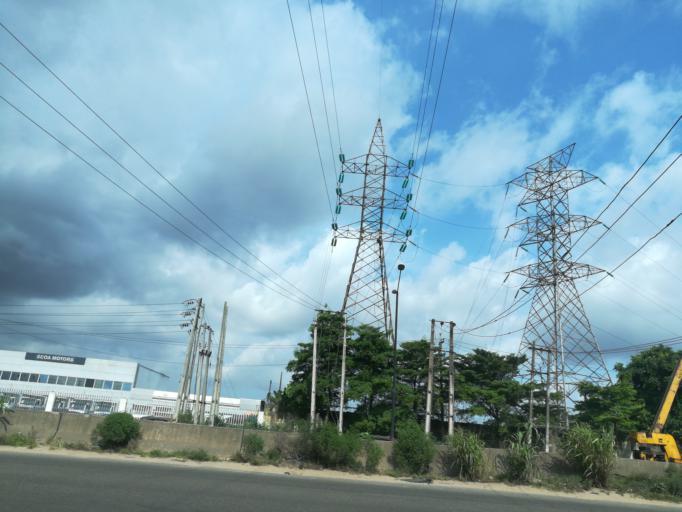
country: NG
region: Lagos
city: Mushin
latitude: 6.5366
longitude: 3.3365
